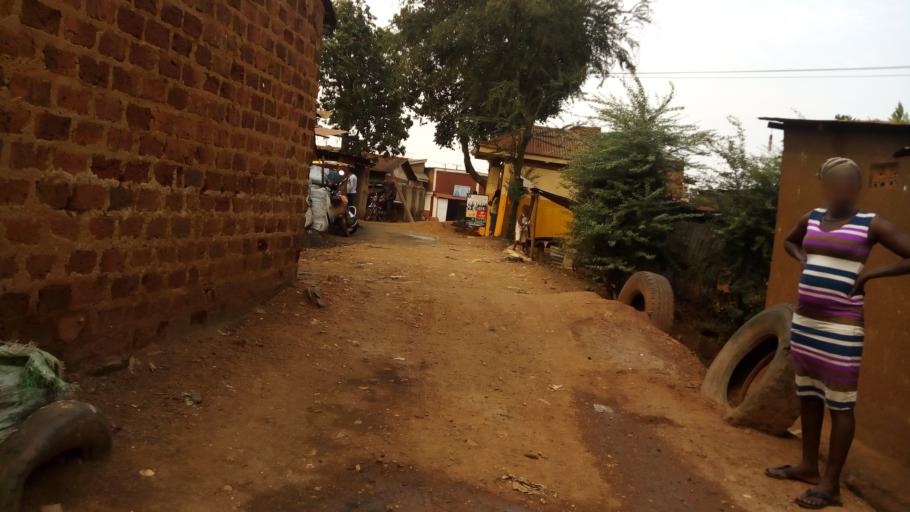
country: UG
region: Central Region
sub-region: Wakiso District
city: Kireka
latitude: 0.3214
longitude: 32.6345
